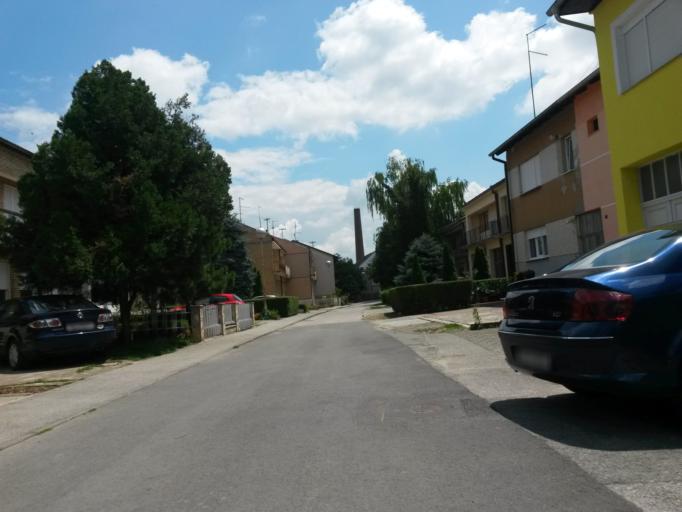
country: HR
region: Osjecko-Baranjska
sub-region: Grad Osijek
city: Osijek
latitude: 45.5552
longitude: 18.7301
